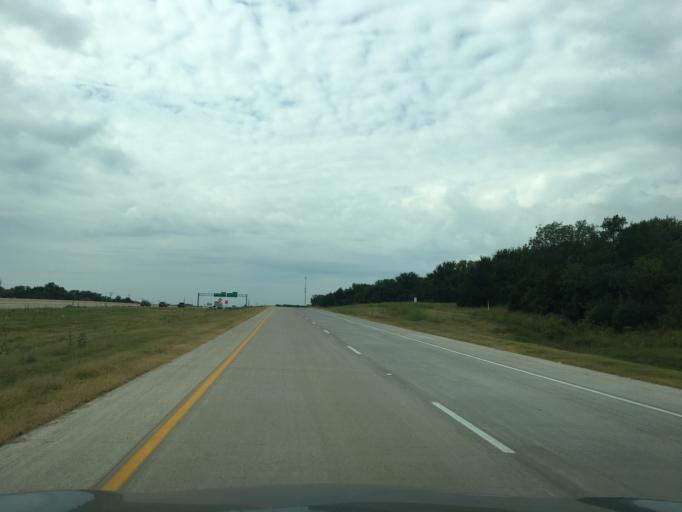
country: US
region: Texas
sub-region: Collin County
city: Anna
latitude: 33.3309
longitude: -96.5896
